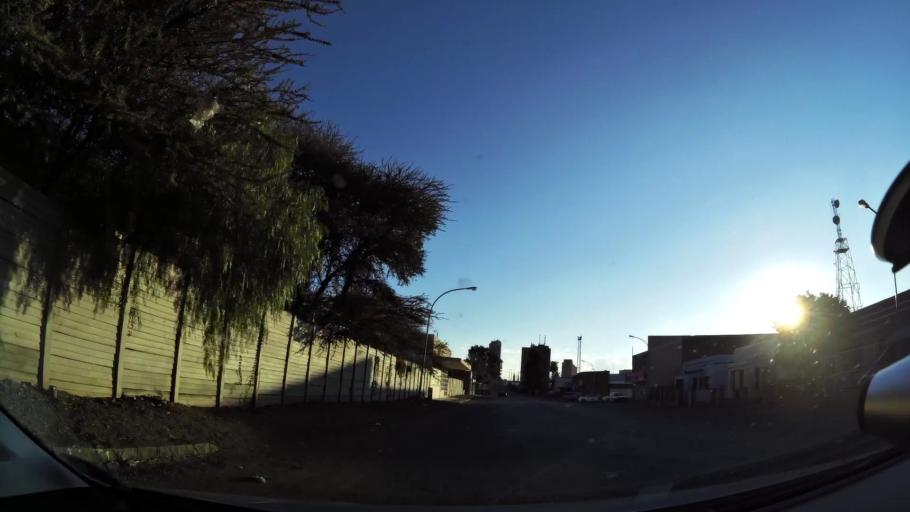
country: ZA
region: Northern Cape
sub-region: Frances Baard District Municipality
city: Kimberley
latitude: -28.7372
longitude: 24.7721
